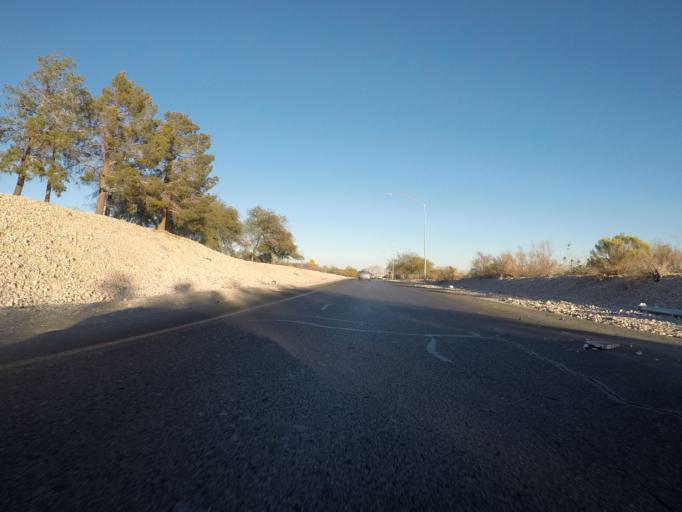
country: US
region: Nevada
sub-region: Clark County
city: Summerlin South
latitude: 36.1772
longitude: -115.2856
